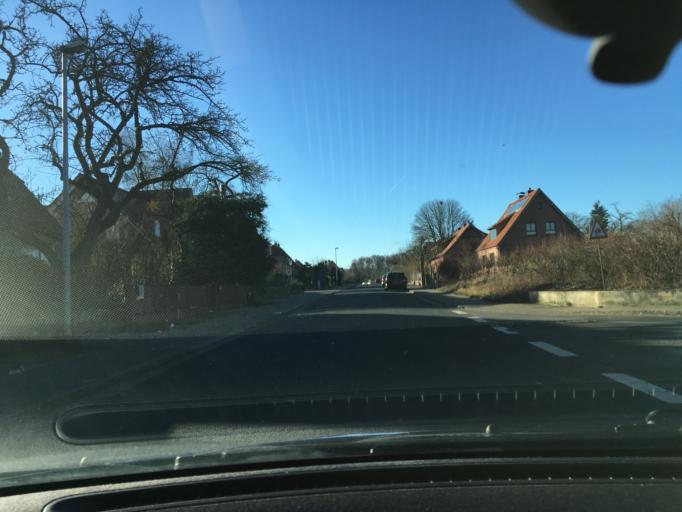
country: DE
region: Lower Saxony
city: Barnstedt
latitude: 53.1432
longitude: 10.3717
